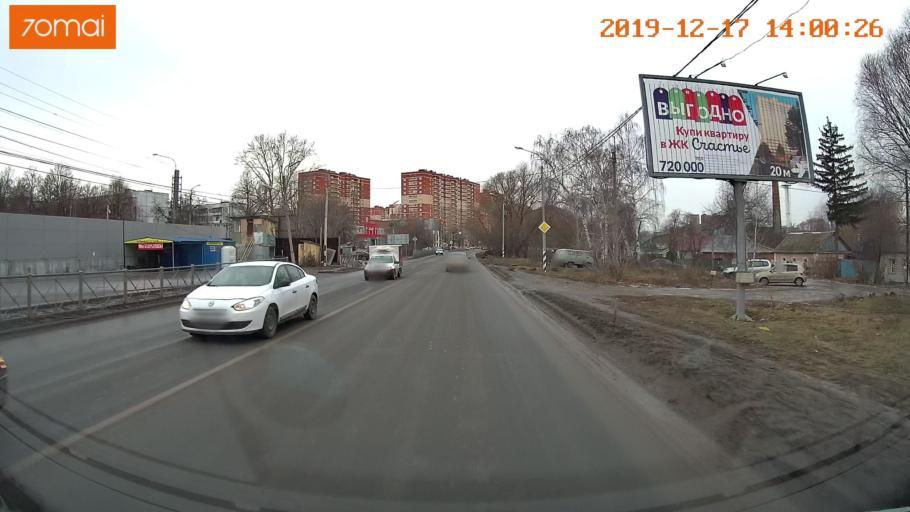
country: RU
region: Rjazan
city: Ryazan'
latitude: 54.6193
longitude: 39.6725
